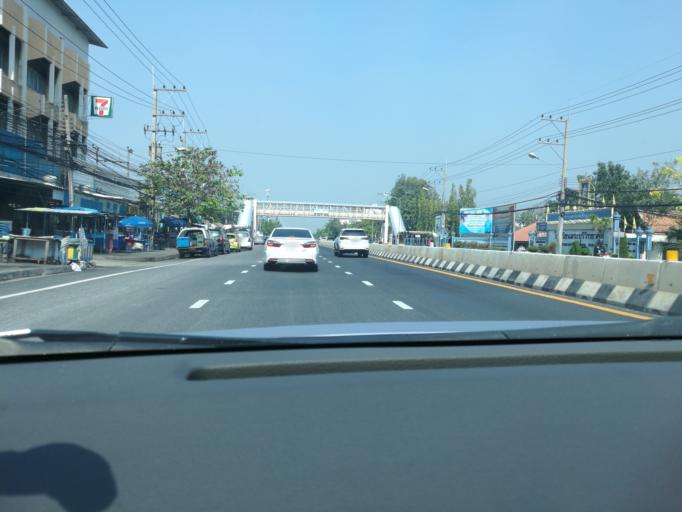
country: TH
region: Sara Buri
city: Saraburi
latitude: 14.5415
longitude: 100.9096
